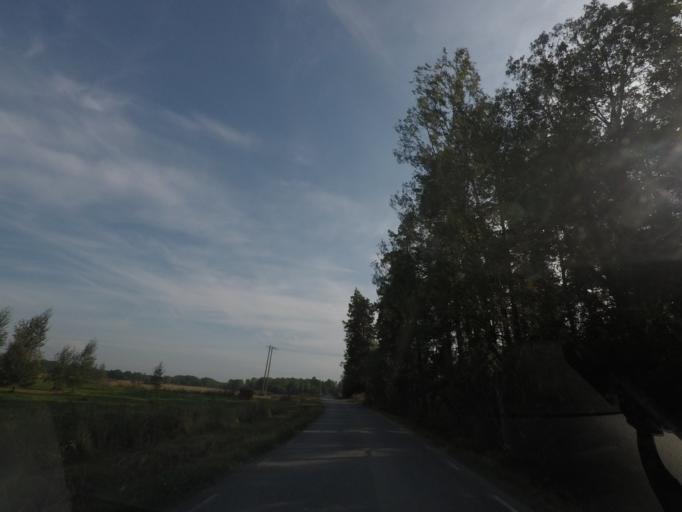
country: SE
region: Vaestmanland
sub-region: Kungsors Kommun
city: Kungsoer
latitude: 59.5201
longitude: 16.1465
